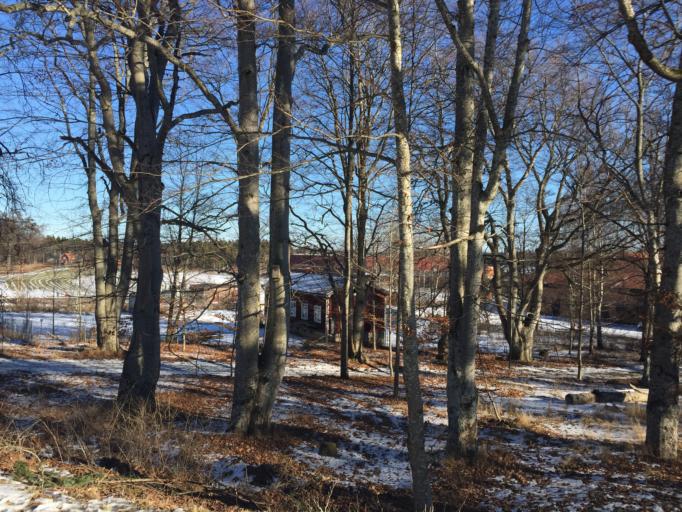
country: SE
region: Stockholm
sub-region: Nykvarns Kommun
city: Nykvarn
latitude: 59.1843
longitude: 17.4308
